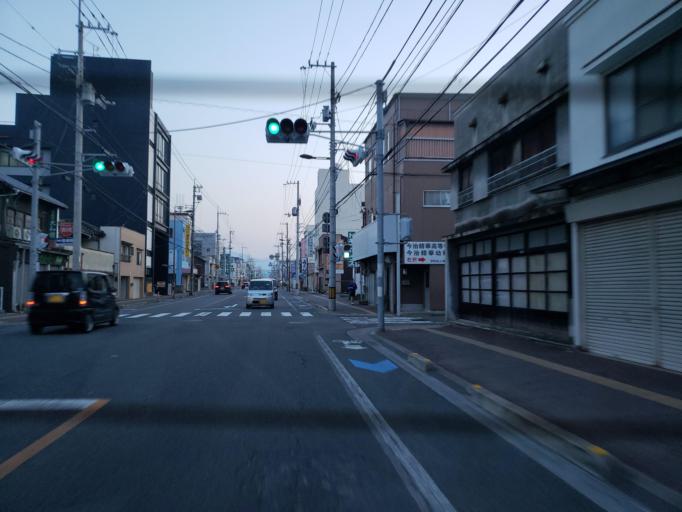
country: JP
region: Ehime
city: Hojo
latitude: 34.0588
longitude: 132.9918
